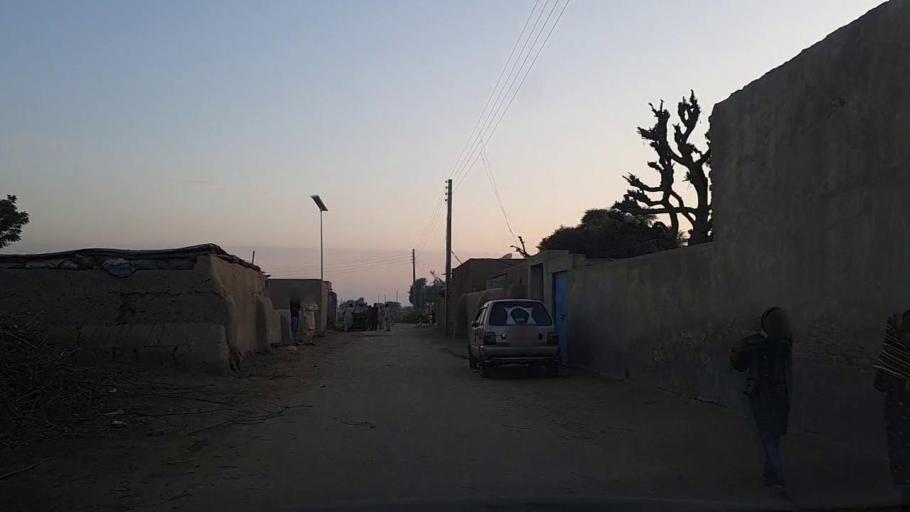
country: PK
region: Sindh
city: Jam Sahib
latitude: 26.4620
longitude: 68.5218
